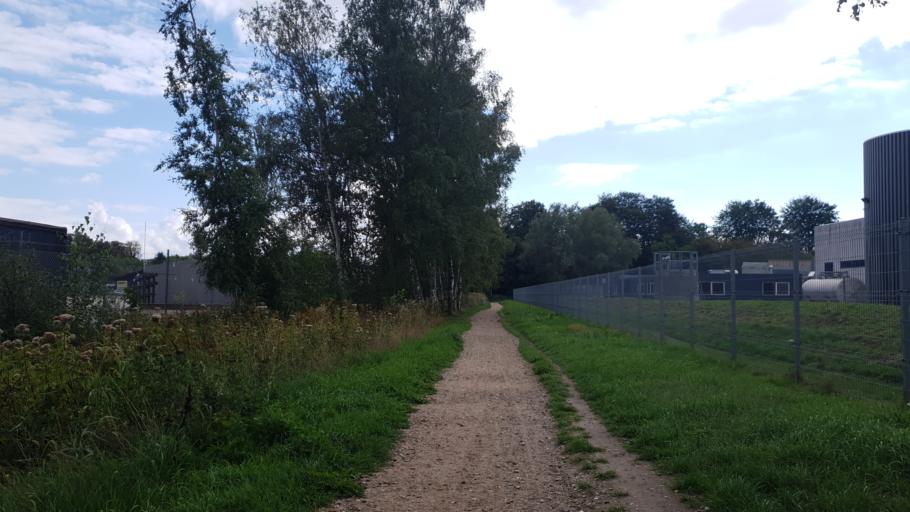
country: DK
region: South Denmark
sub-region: Fredericia Kommune
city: Snoghoj
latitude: 55.5529
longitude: 9.7230
